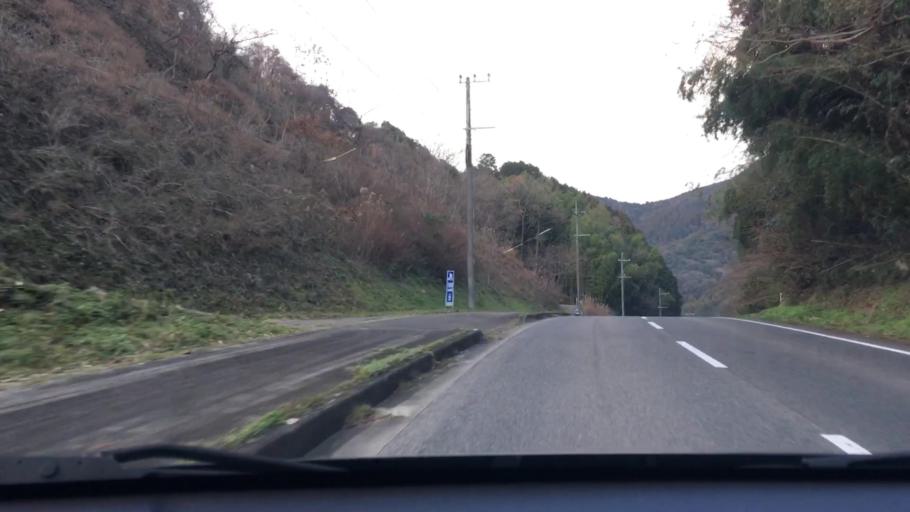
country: JP
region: Oita
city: Bungo-Takada-shi
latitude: 33.4761
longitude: 131.3849
